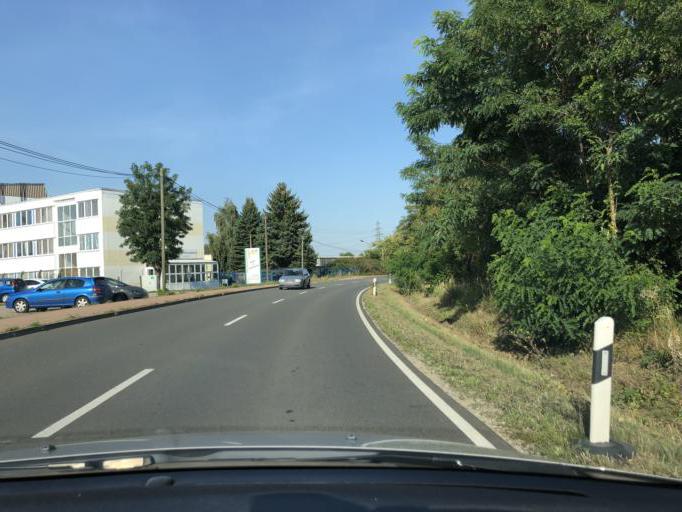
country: DE
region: Saxony-Anhalt
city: Beuna
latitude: 51.3089
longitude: 11.9444
